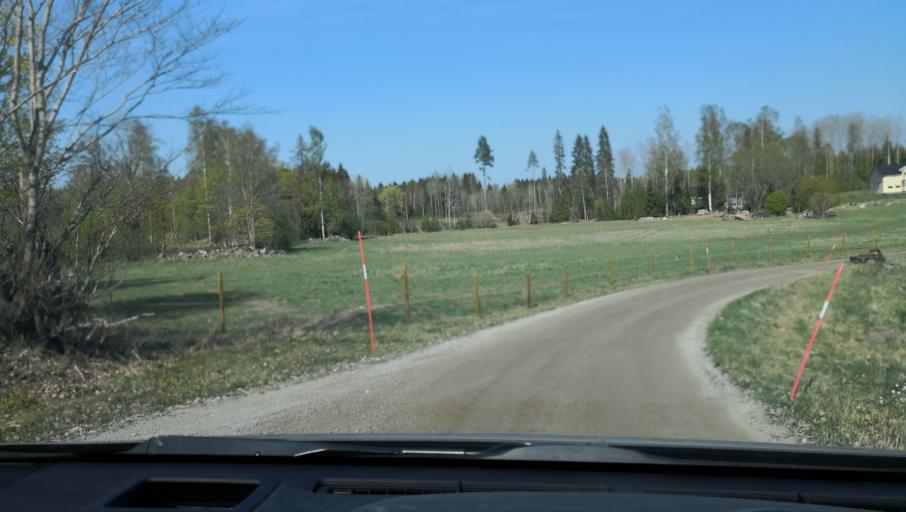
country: SE
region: Vaestmanland
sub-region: Sala Kommun
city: Sala
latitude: 60.0085
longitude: 16.7268
